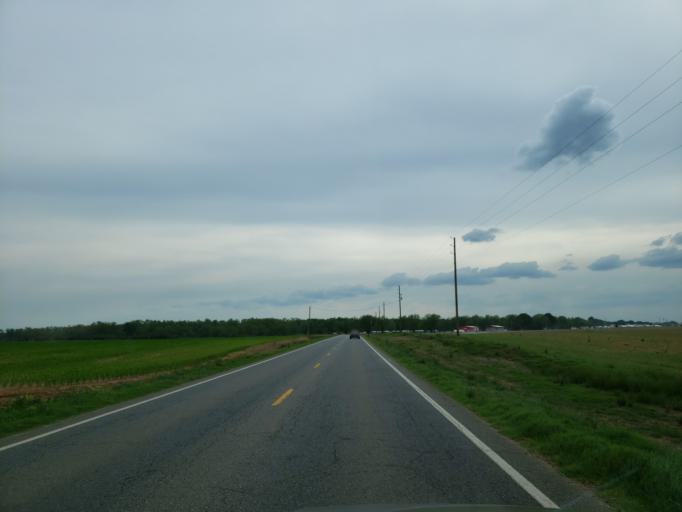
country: US
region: Georgia
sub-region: Macon County
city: Montezuma
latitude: 32.3601
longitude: -83.9608
